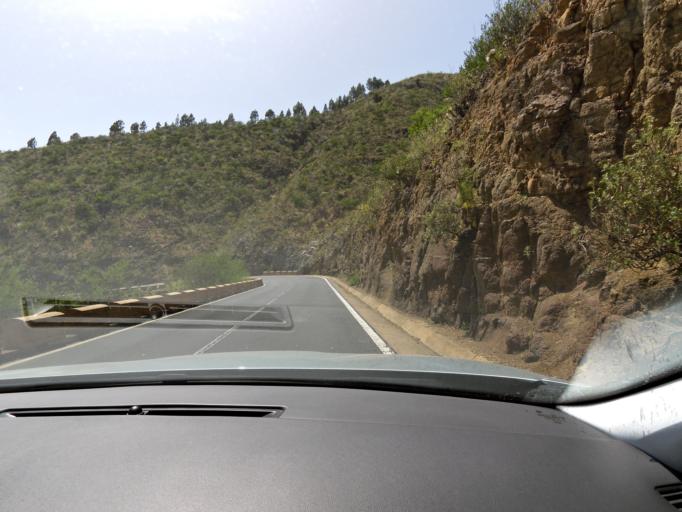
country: ES
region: Canary Islands
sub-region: Provincia de Santa Cruz de Tenerife
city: Santiago del Teide
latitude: 28.3095
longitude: -16.8093
